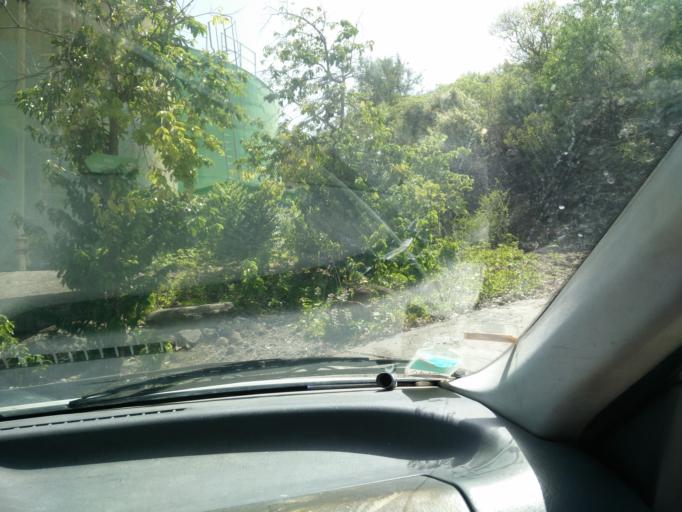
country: GP
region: Guadeloupe
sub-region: Guadeloupe
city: Terre-de-Bas
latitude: 15.8535
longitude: -61.6260
